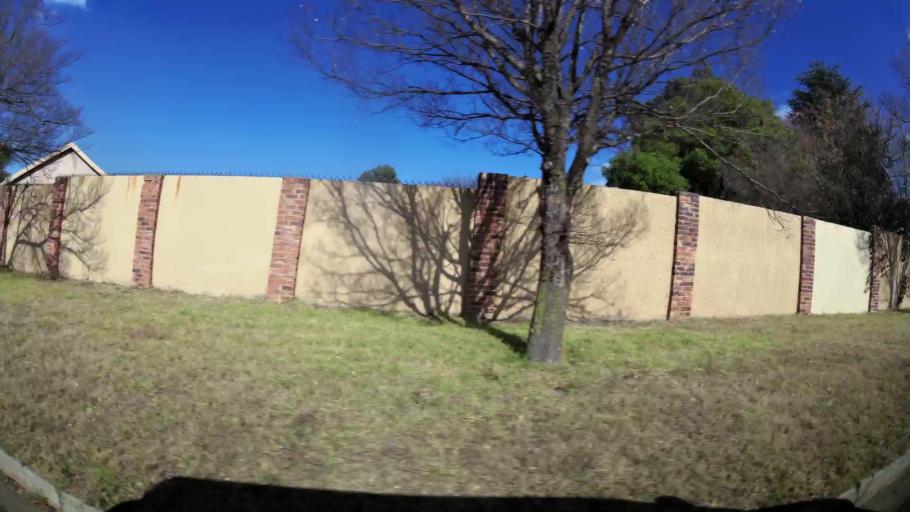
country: ZA
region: Gauteng
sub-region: Ekurhuleni Metropolitan Municipality
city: Benoni
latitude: -26.1412
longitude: 28.3479
